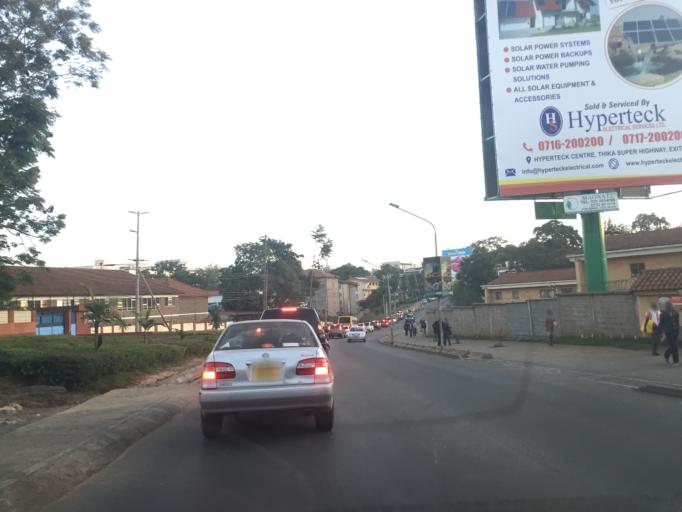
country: KE
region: Nairobi Area
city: Nairobi
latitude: -1.2678
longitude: 36.8015
